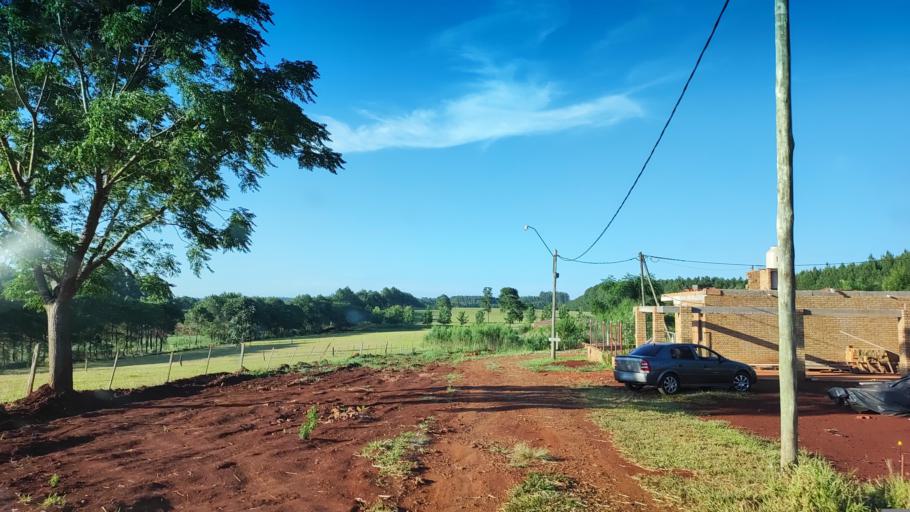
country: AR
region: Misiones
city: Capiovi
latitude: -26.9310
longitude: -55.0694
